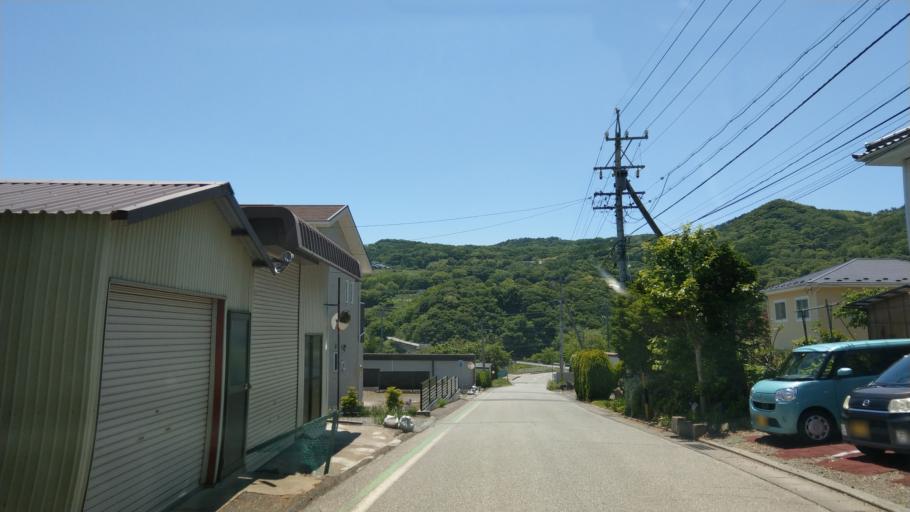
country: JP
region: Nagano
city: Komoro
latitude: 36.3336
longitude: 138.3926
